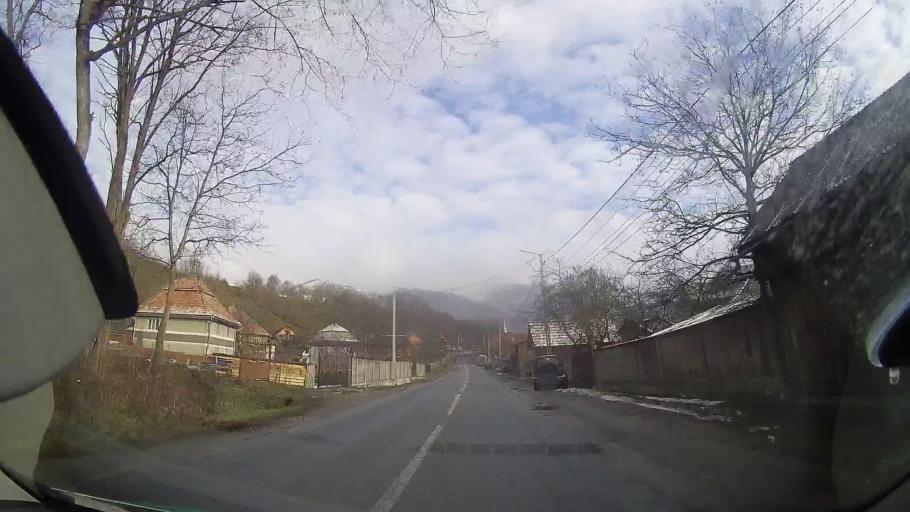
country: RO
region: Alba
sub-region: Comuna Lupsa
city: Lupsa
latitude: 46.3778
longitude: 23.2207
